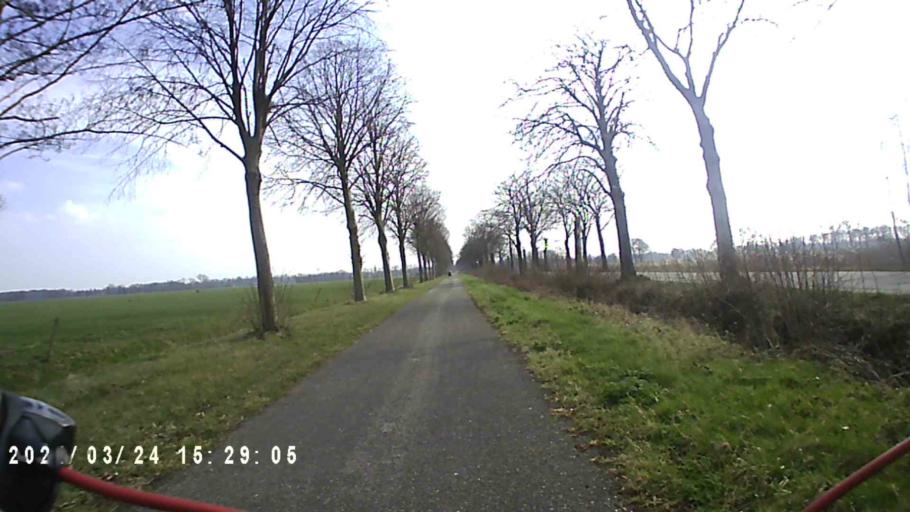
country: NL
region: Friesland
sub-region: Gemeente Heerenveen
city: Jubbega
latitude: 53.0136
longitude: 6.1150
